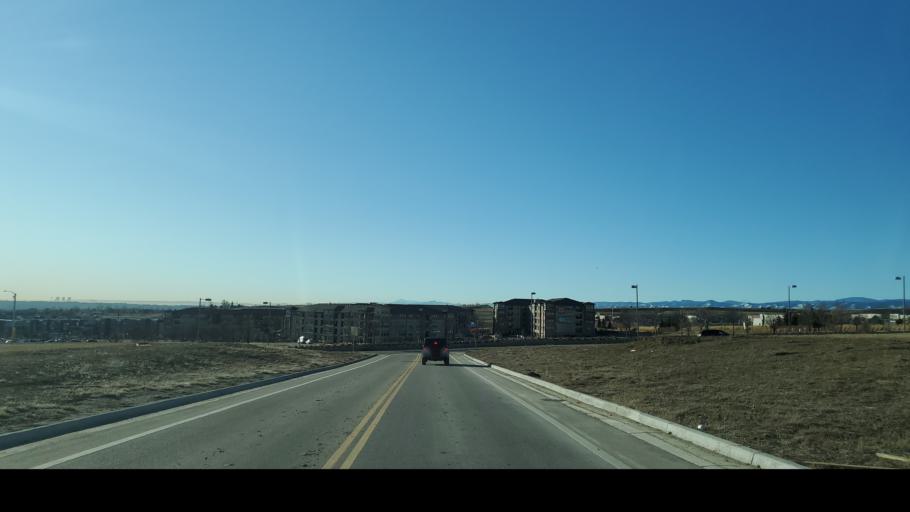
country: US
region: Colorado
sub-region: Broomfield County
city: Broomfield
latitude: 39.9100
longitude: -105.0946
